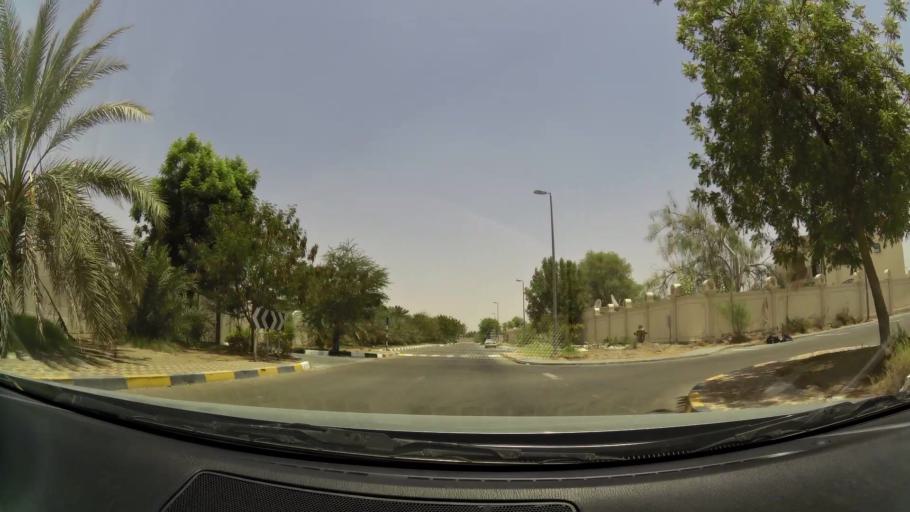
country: OM
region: Al Buraimi
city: Al Buraymi
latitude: 24.2875
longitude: 55.7405
